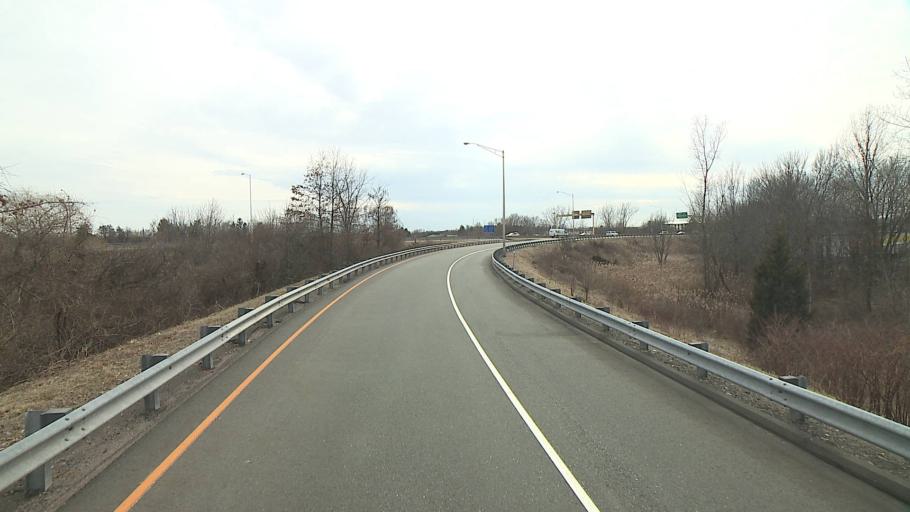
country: US
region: Connecticut
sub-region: Hartford County
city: Glastonbury
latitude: 41.7264
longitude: -72.6130
